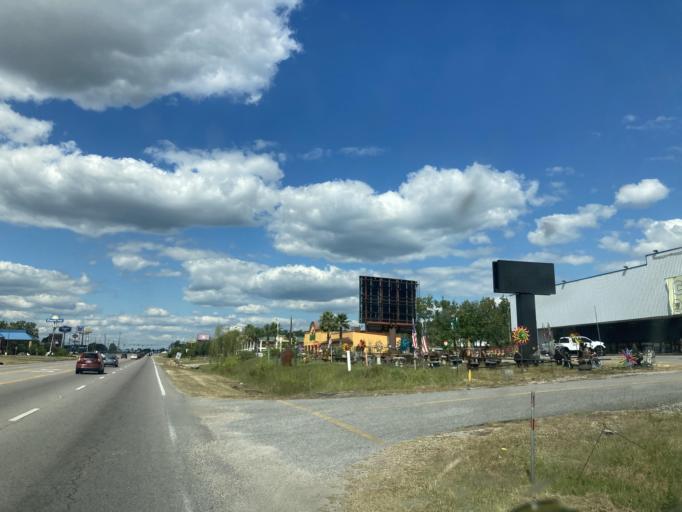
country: US
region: Mississippi
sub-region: Jackson County
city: Gulf Hills
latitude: 30.4462
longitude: -88.8396
